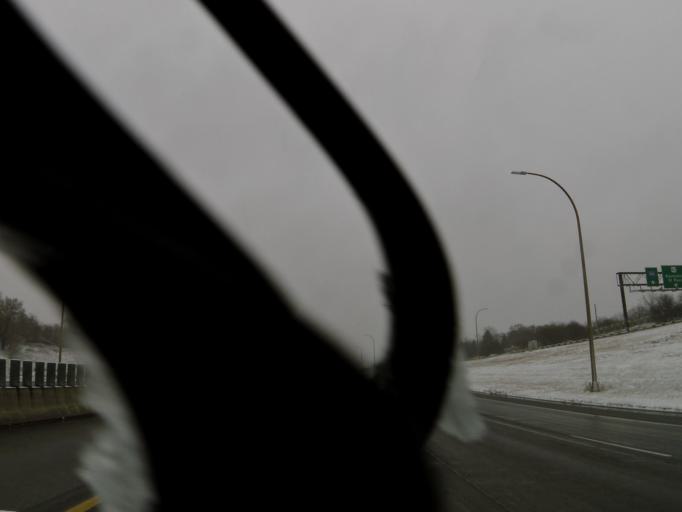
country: US
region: Minnesota
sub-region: Dakota County
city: Inver Grove Heights
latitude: 44.8753
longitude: -93.0743
